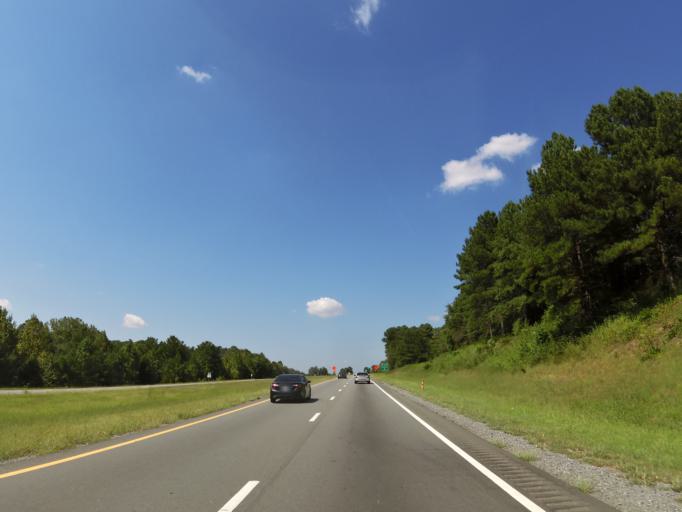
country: US
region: North Carolina
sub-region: Lincoln County
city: Lincolnton
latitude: 35.4086
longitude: -81.2102
